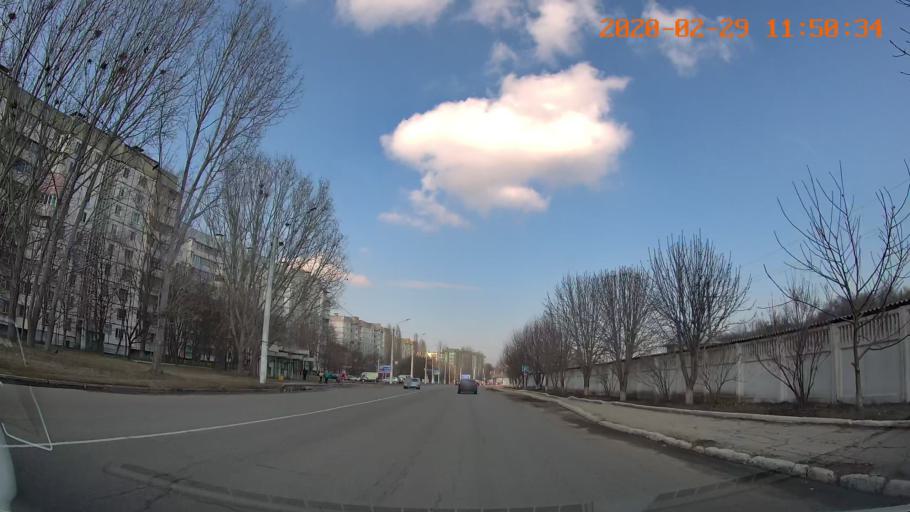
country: MD
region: Telenesti
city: Ribnita
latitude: 47.7588
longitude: 28.9905
